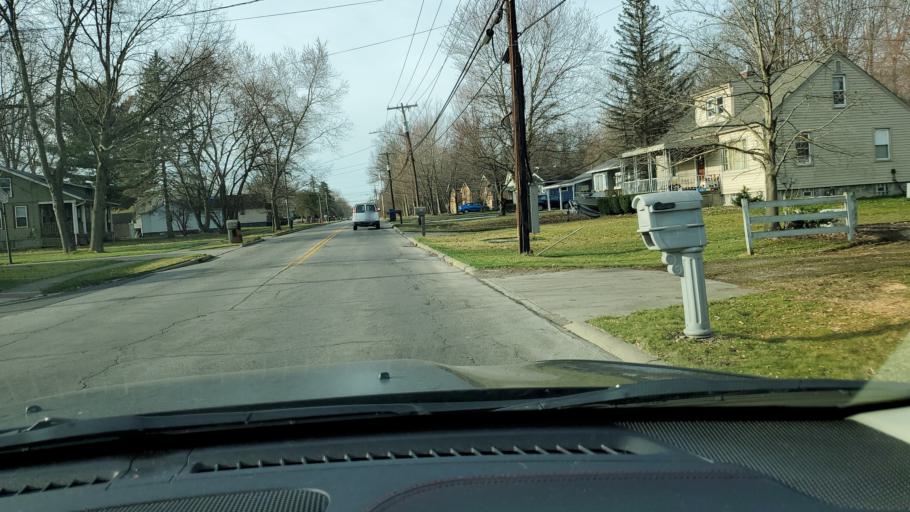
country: US
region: Ohio
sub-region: Trumbull County
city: Bolindale
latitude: 41.2020
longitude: -80.7661
